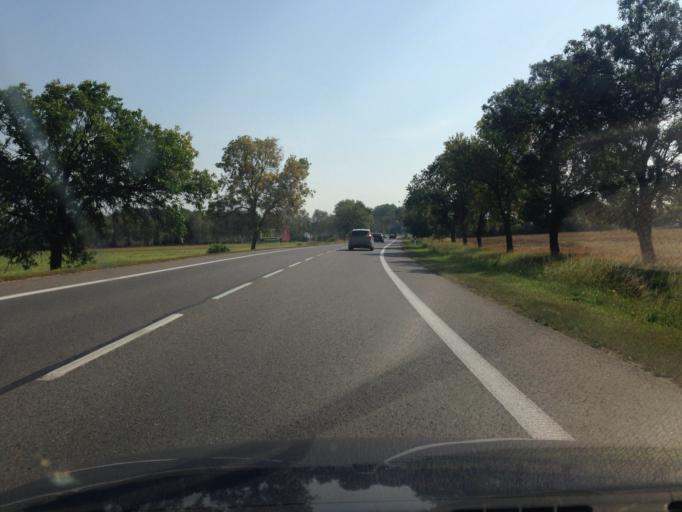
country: PL
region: Masovian Voivodeship
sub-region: Powiat plonski
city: Plonsk
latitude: 52.6181
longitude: 20.3270
